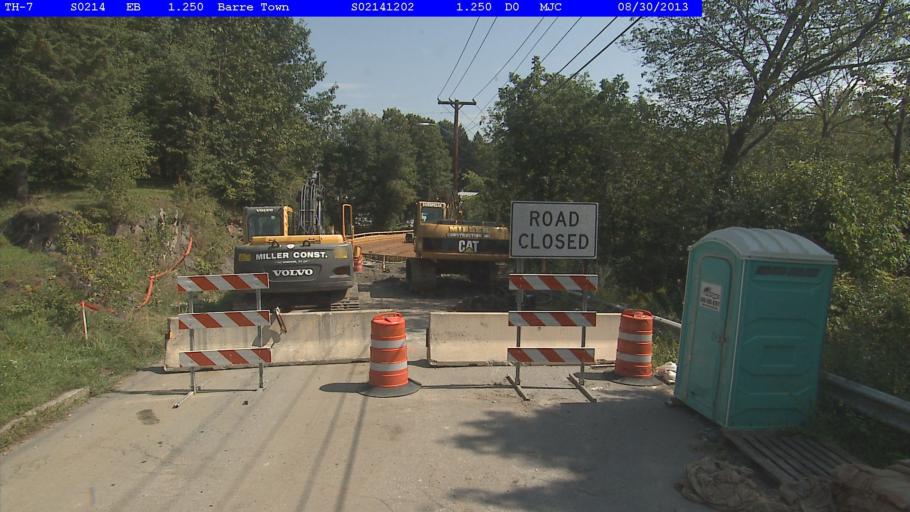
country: US
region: Vermont
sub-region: Washington County
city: South Barre
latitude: 44.1780
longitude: -72.5074
